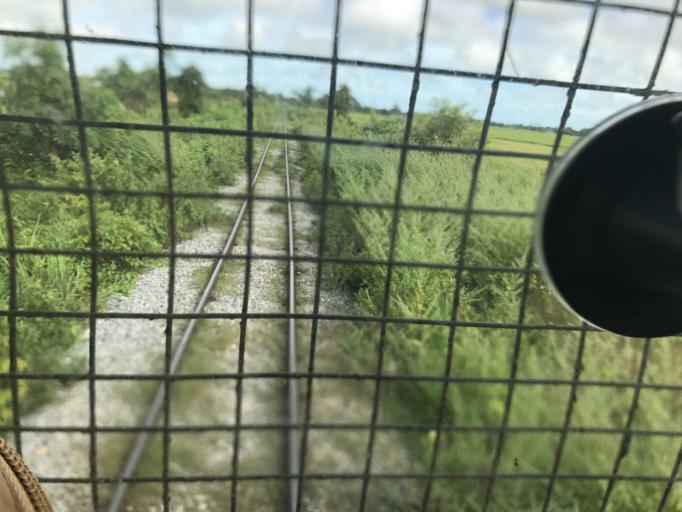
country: MM
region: Bago
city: Letpandan
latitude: 18.0251
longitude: 95.6976
